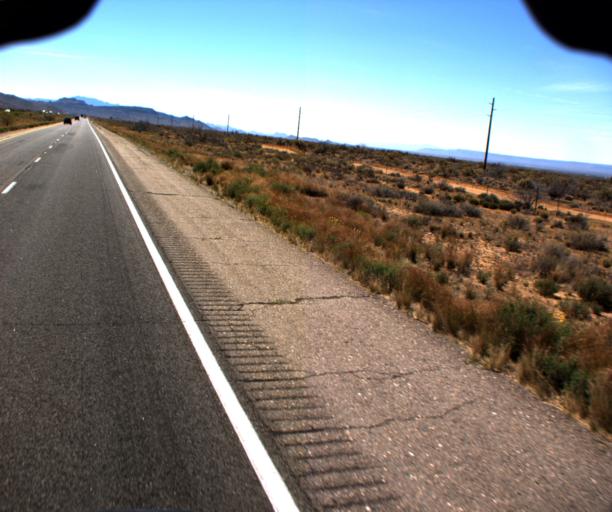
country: US
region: Arizona
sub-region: Mohave County
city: Golden Valley
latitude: 35.2944
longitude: -114.1854
